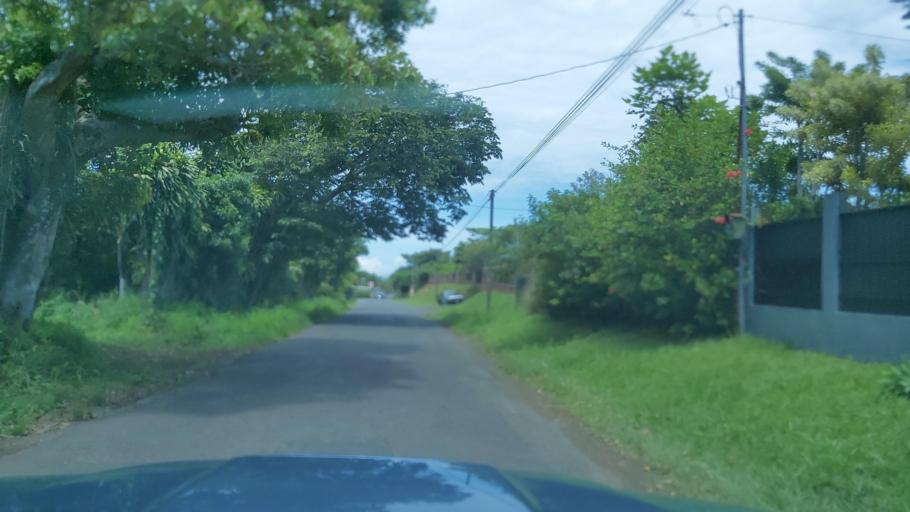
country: CR
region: Alajuela
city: San Juan
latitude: 10.1001
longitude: -84.3363
